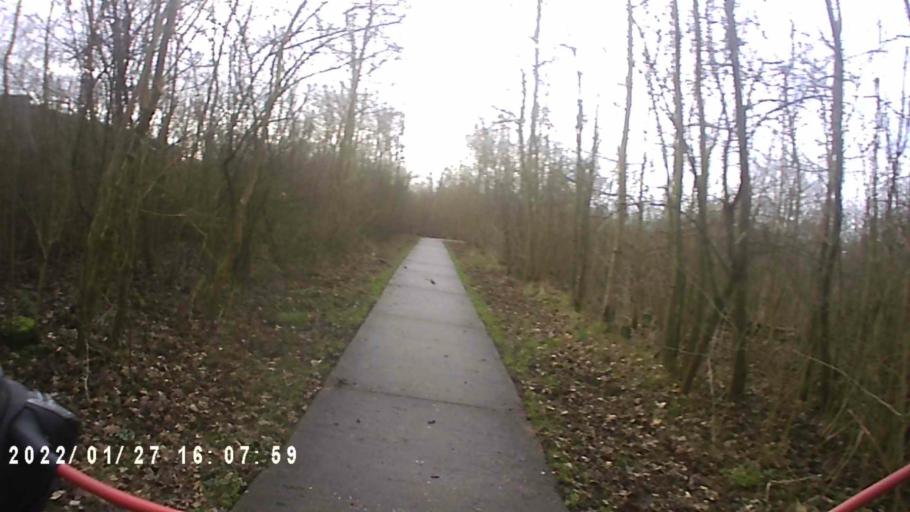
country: NL
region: Friesland
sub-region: Gemeente Dongeradeel
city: Anjum
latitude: 53.3821
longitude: 6.0866
